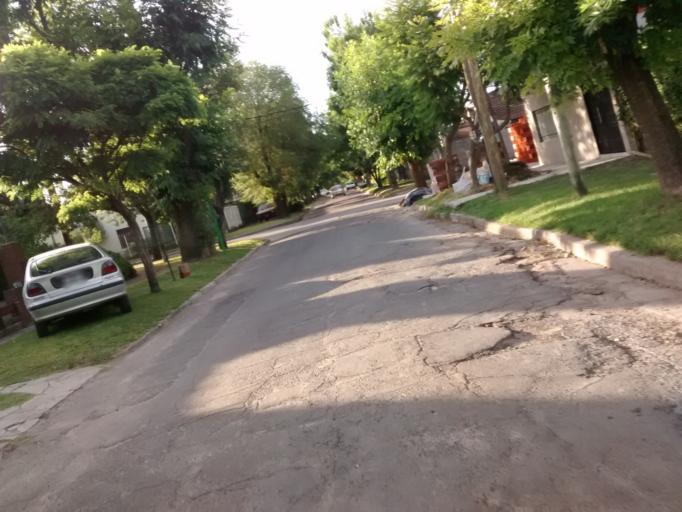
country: AR
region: Buenos Aires
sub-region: Partido de La Plata
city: La Plata
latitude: -34.8714
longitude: -58.0871
